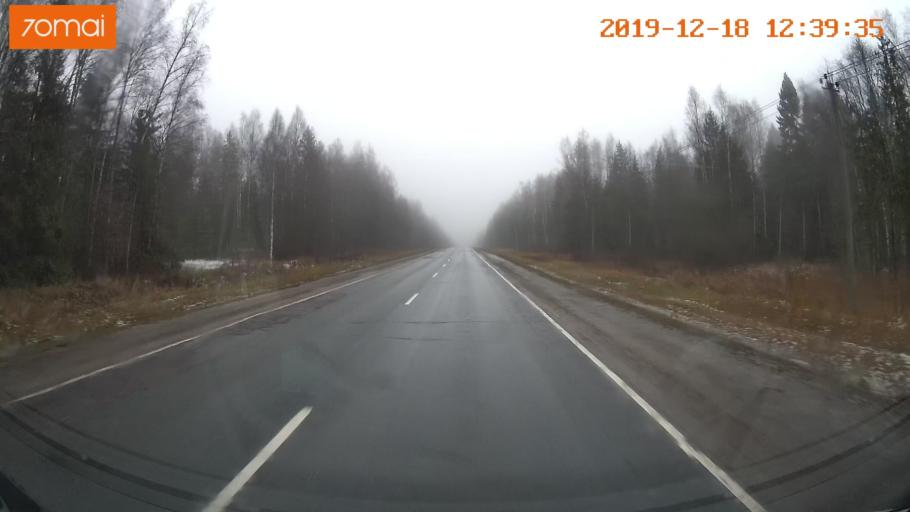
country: RU
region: Moskovskaya
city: Vysokovsk
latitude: 56.1668
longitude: 36.6123
